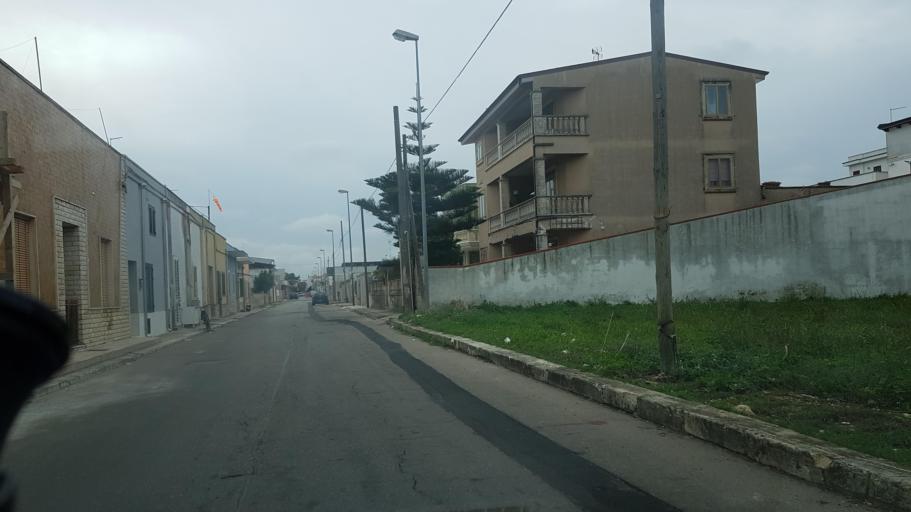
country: IT
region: Apulia
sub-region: Provincia di Brindisi
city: Cellino San Marco
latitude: 40.4722
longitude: 17.9600
